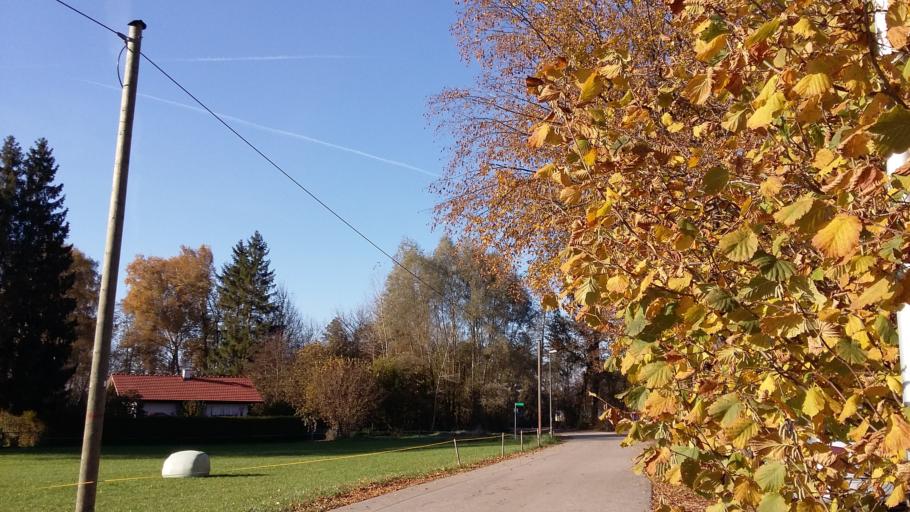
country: DE
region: Bavaria
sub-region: Upper Bavaria
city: Riedering
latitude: 47.8555
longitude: 12.2296
